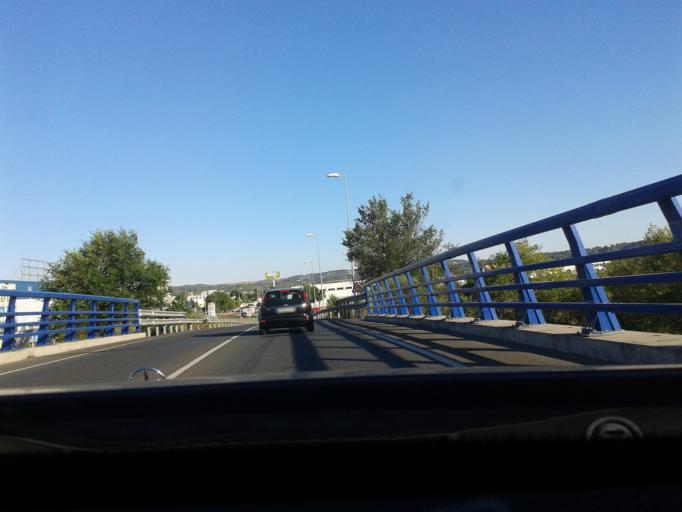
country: ES
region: Madrid
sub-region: Provincia de Madrid
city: Alcala de Henares
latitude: 40.4928
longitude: -3.3886
